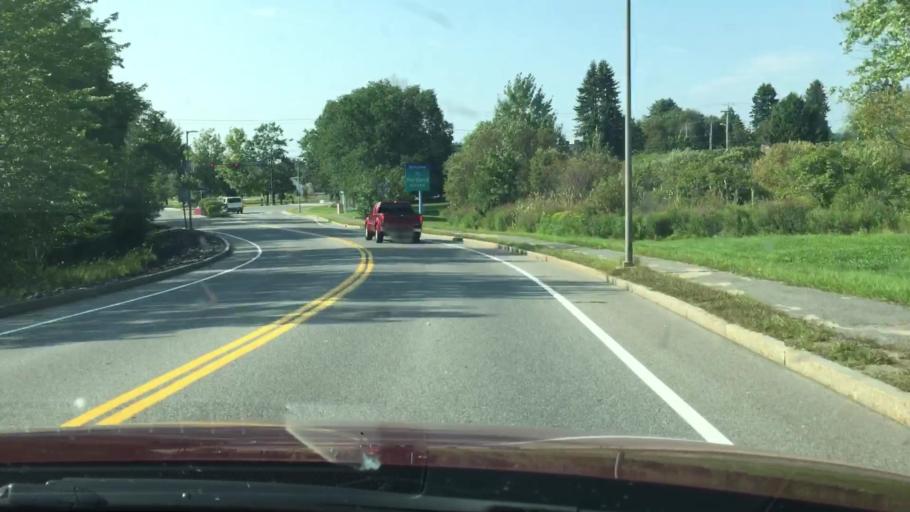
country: US
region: Maine
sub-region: Cumberland County
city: South Portland Gardens
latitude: 43.6521
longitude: -70.3175
